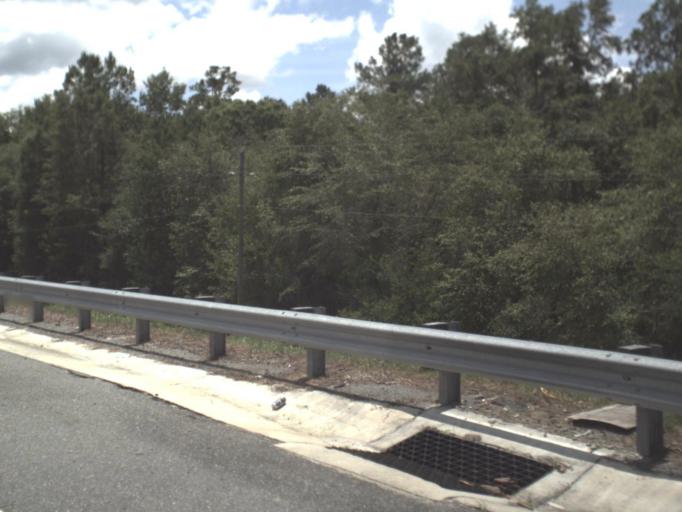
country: US
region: Florida
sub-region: Suwannee County
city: Wellborn
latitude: 30.3247
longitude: -82.7364
